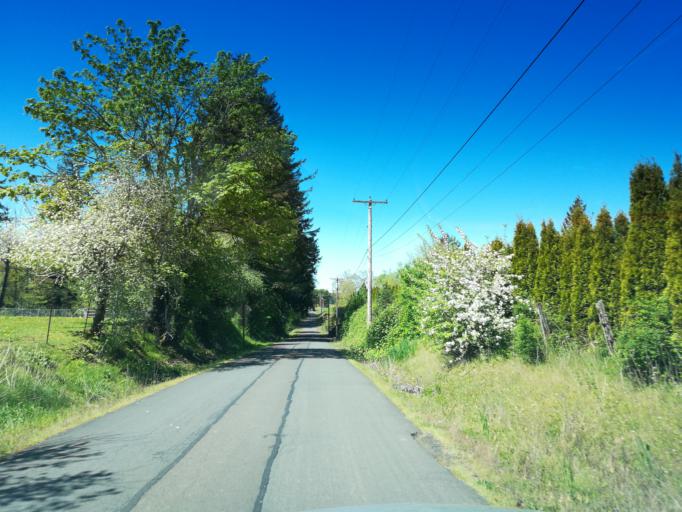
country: US
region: Oregon
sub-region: Multnomah County
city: Troutdale
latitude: 45.5045
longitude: -122.3690
